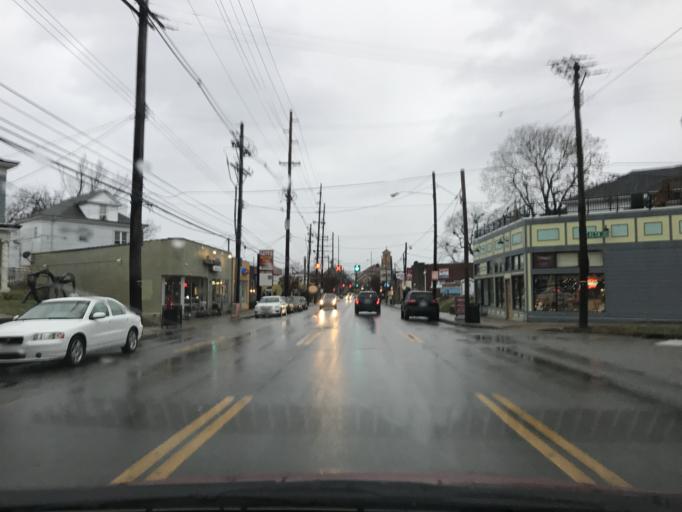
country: US
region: Kentucky
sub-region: Jefferson County
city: Audubon Park
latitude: 38.2311
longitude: -85.7057
